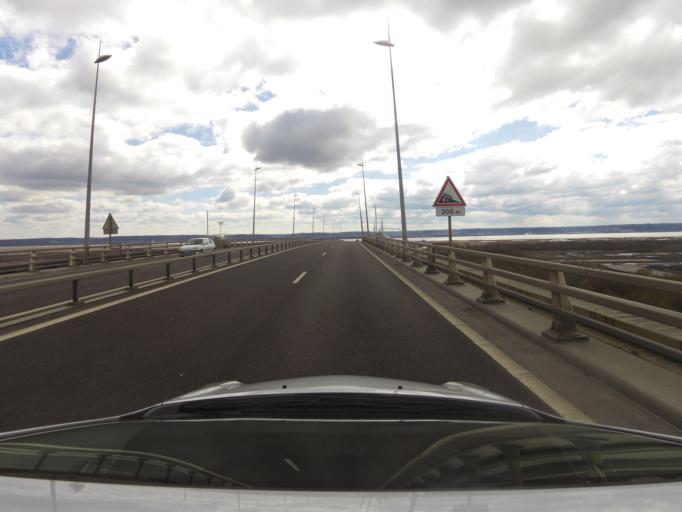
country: FR
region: Haute-Normandie
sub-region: Departement de la Seine-Maritime
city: Rogerville
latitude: 49.4657
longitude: 0.2743
